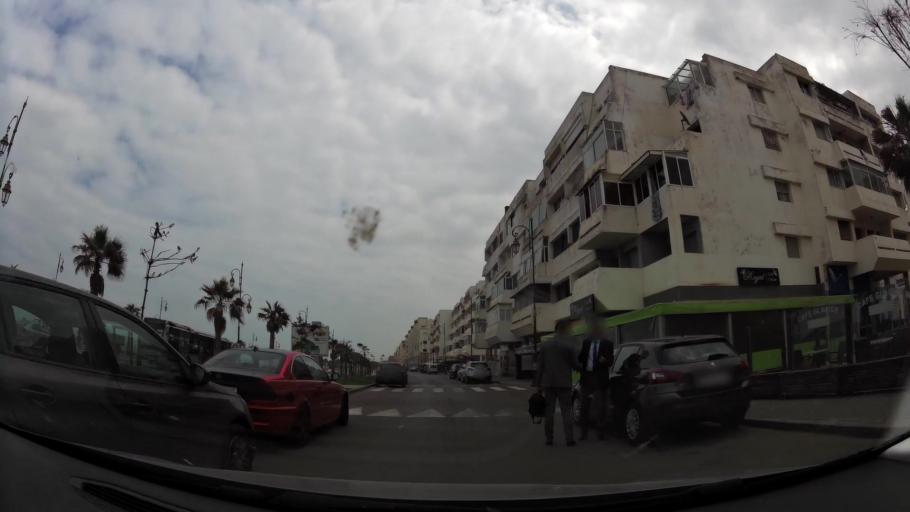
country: MA
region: Rabat-Sale-Zemmour-Zaer
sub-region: Rabat
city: Rabat
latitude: 33.9930
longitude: -6.8821
